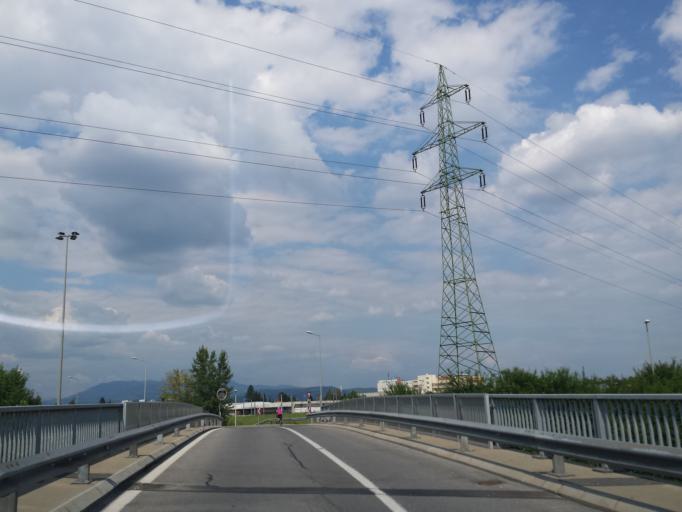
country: AT
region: Styria
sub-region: Politischer Bezirk Graz-Umgebung
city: Feldkirchen bei Graz
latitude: 47.0310
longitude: 15.4259
